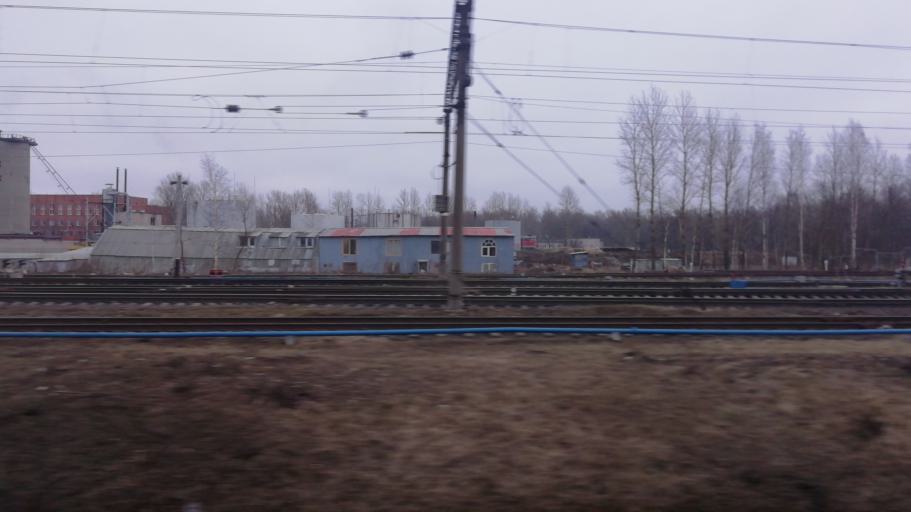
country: RU
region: St.-Petersburg
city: Kupchino
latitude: 59.8819
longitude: 30.3478
